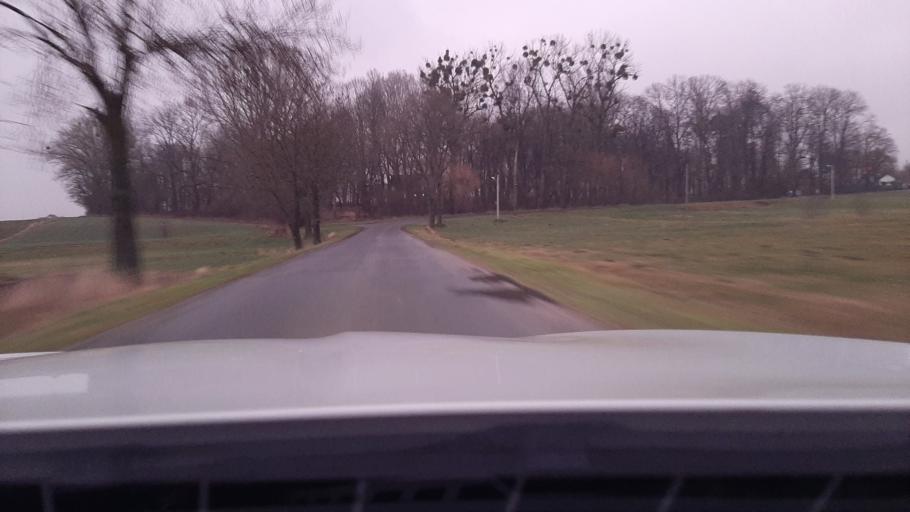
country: PL
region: Lublin Voivodeship
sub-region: Powiat lubelski
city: Garbow
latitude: 51.3518
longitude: 22.3842
